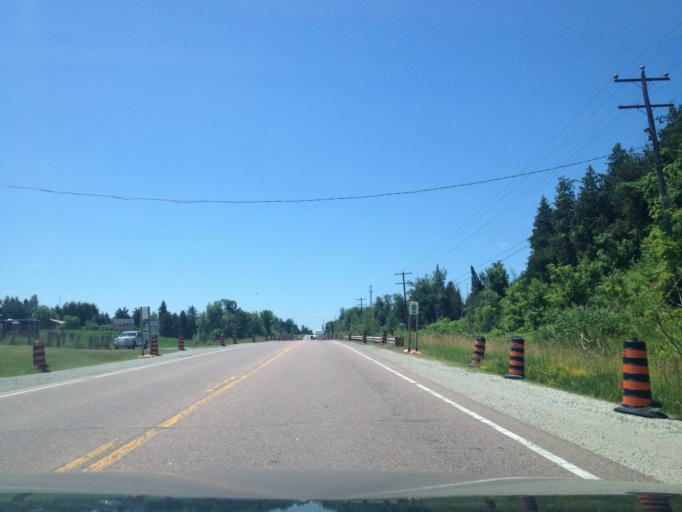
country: CA
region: Ontario
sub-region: Halton
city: Milton
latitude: 43.6633
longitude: -79.9997
